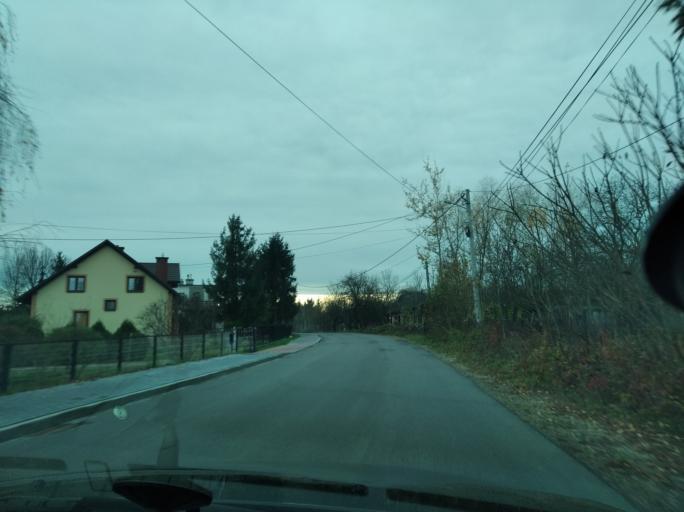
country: PL
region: Subcarpathian Voivodeship
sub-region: Powiat lancucki
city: Czarna
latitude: 50.0978
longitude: 22.1989
